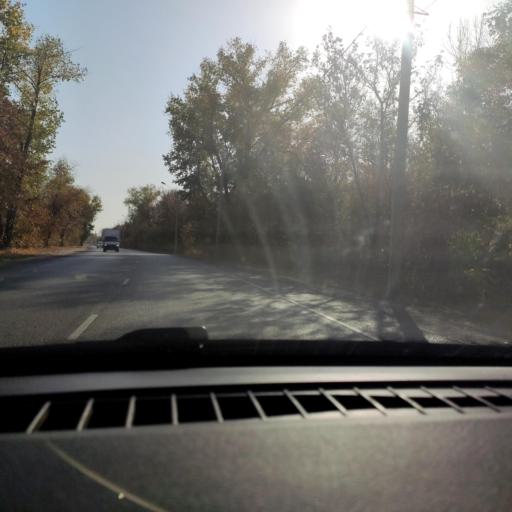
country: RU
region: Voronezj
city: Voronezh
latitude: 51.6007
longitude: 39.1772
